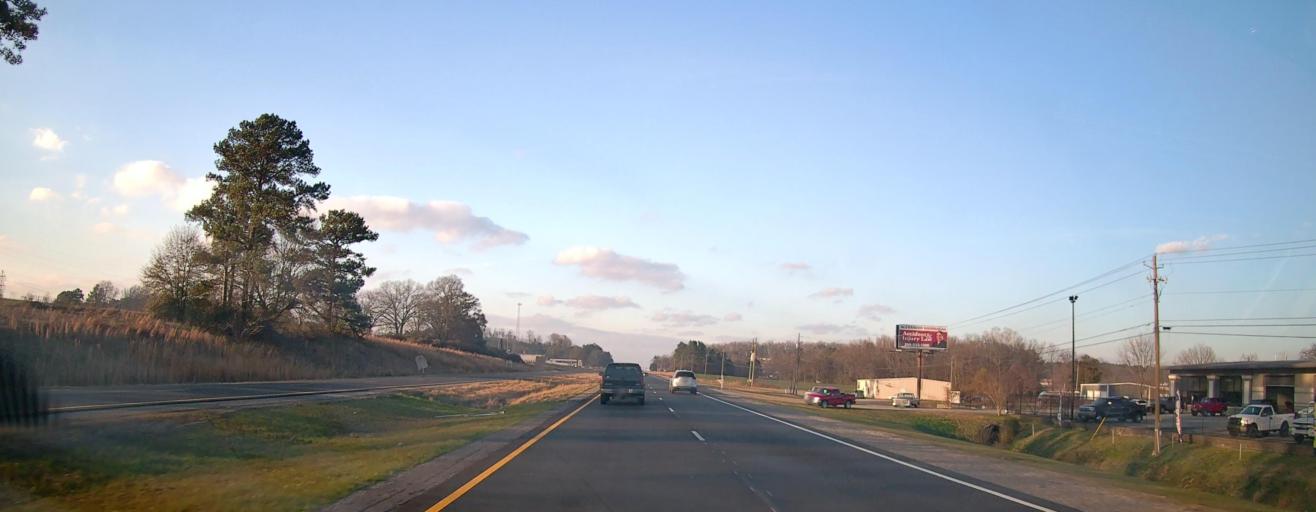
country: US
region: Alabama
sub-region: Calhoun County
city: Alexandria
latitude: 33.7448
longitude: -85.8848
